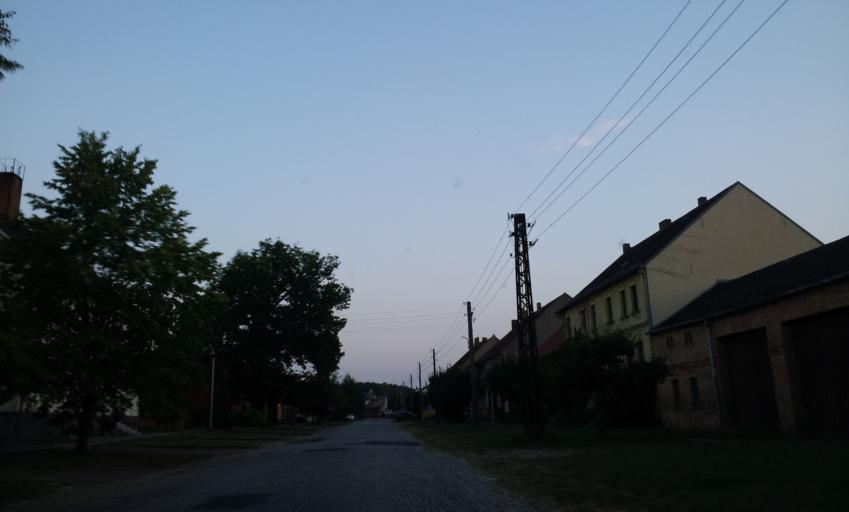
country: DE
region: Brandenburg
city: Treuenbrietzen
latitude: 52.0741
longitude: 12.9428
